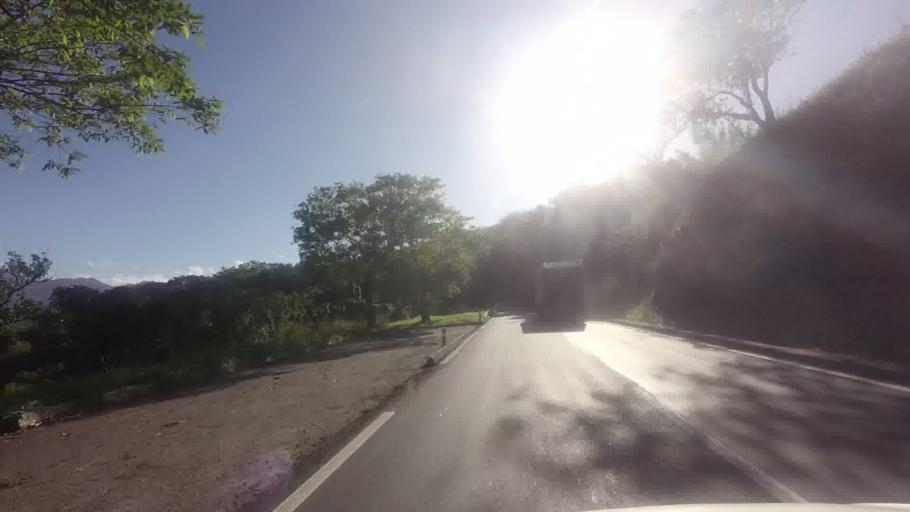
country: BR
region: Rio de Janeiro
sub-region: Petropolis
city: Petropolis
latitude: -22.5872
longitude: -43.2733
